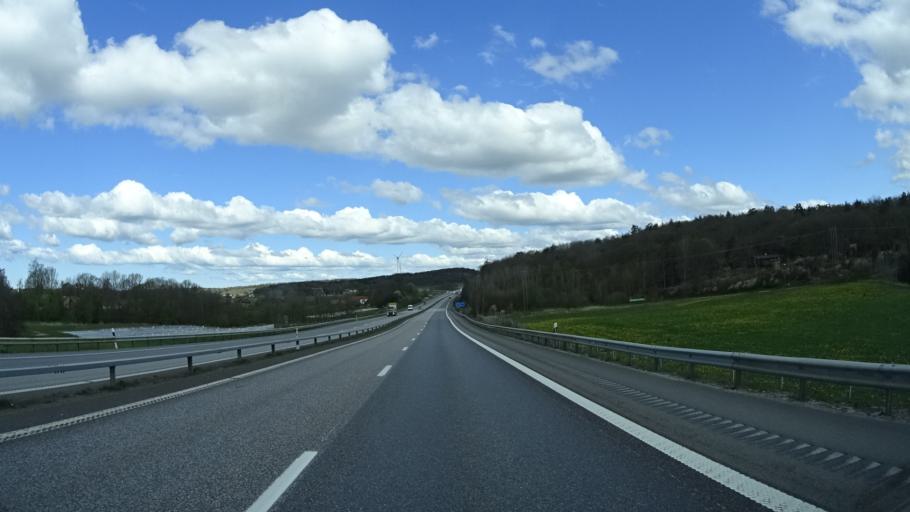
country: SE
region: Halland
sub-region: Kungsbacka Kommun
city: Frillesas
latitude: 57.3152
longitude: 12.2107
